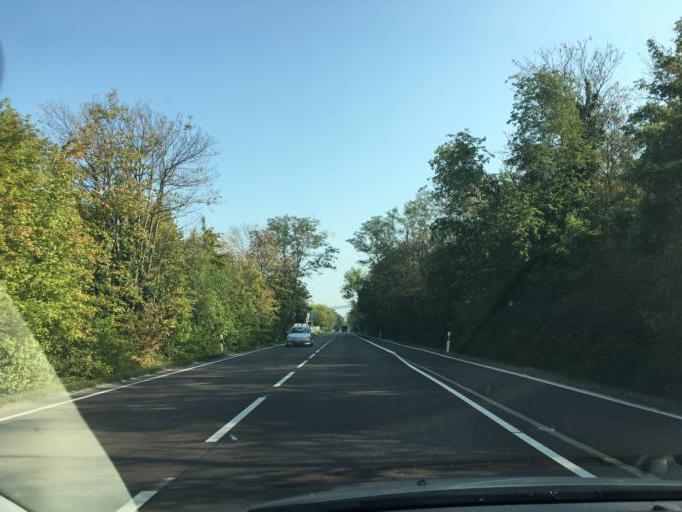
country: DE
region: Saxony-Anhalt
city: Bernburg
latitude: 51.8098
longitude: 11.7403
